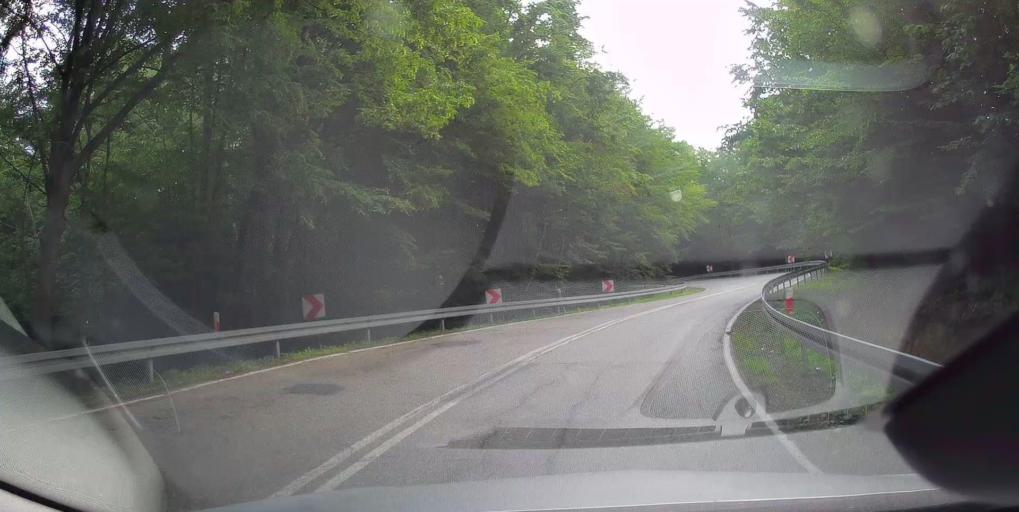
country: PL
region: Lesser Poland Voivodeship
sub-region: Powiat tarnowski
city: Zakliczyn
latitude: 49.7696
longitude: 20.7771
